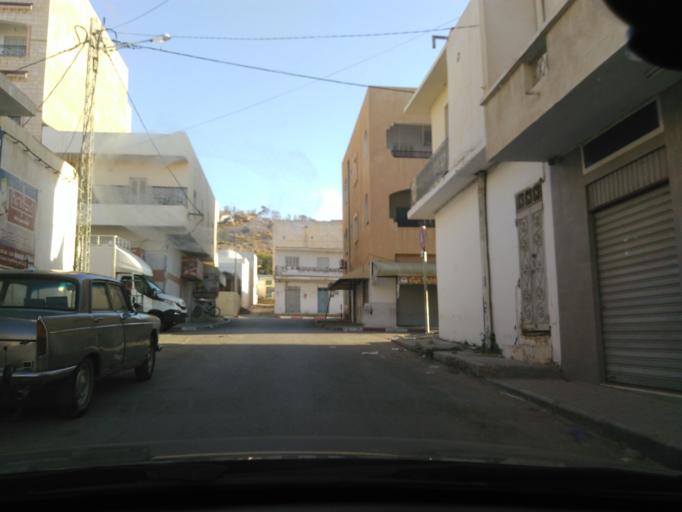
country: TN
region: Tataouine
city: Tataouine
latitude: 32.9273
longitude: 10.4499
